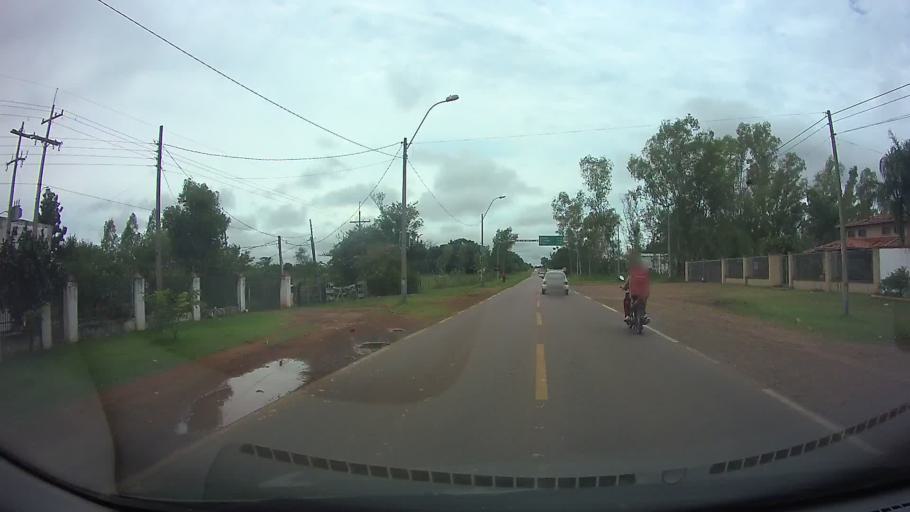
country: PY
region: Paraguari
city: Carapegua
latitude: -25.7735
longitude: -57.2308
